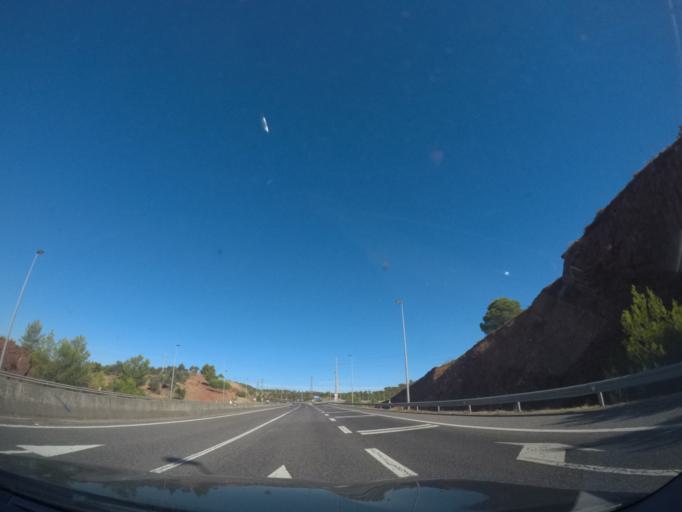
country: PT
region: Faro
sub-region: Portimao
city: Portimao
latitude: 37.1764
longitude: -8.5258
